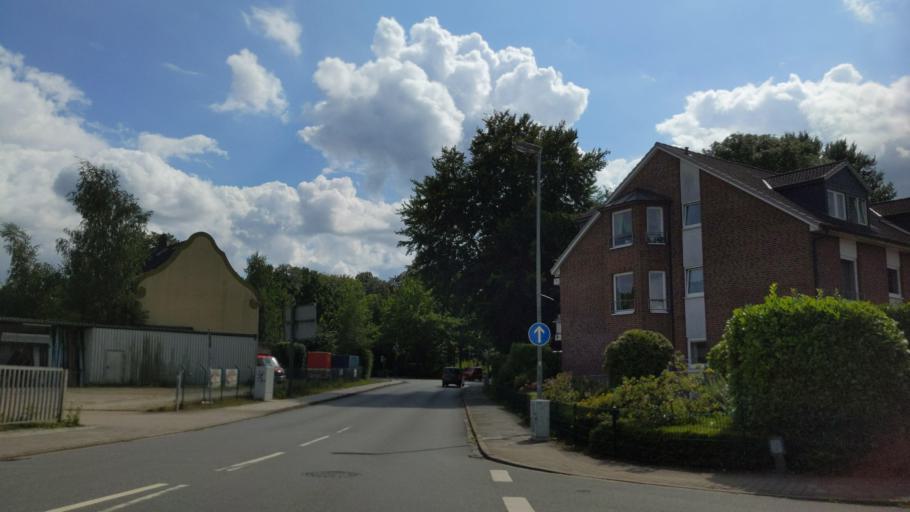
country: DE
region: Schleswig-Holstein
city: Reinfeld
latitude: 53.8305
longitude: 10.4920
